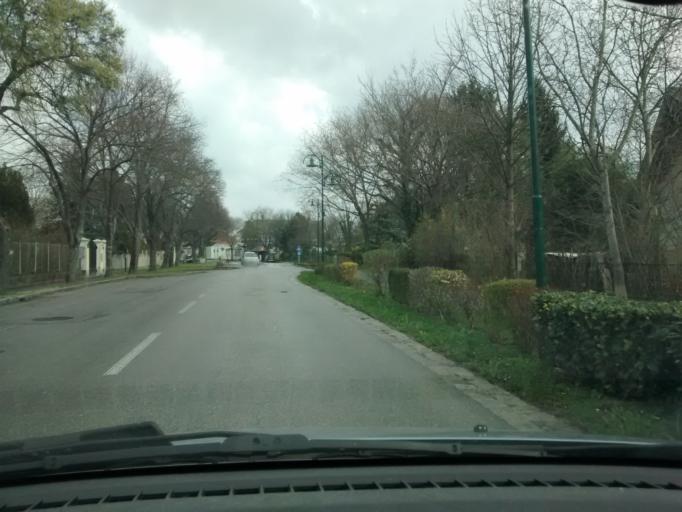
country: AT
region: Lower Austria
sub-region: Politischer Bezirk Modling
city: Biedermannsdorf
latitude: 48.0810
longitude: 16.3521
